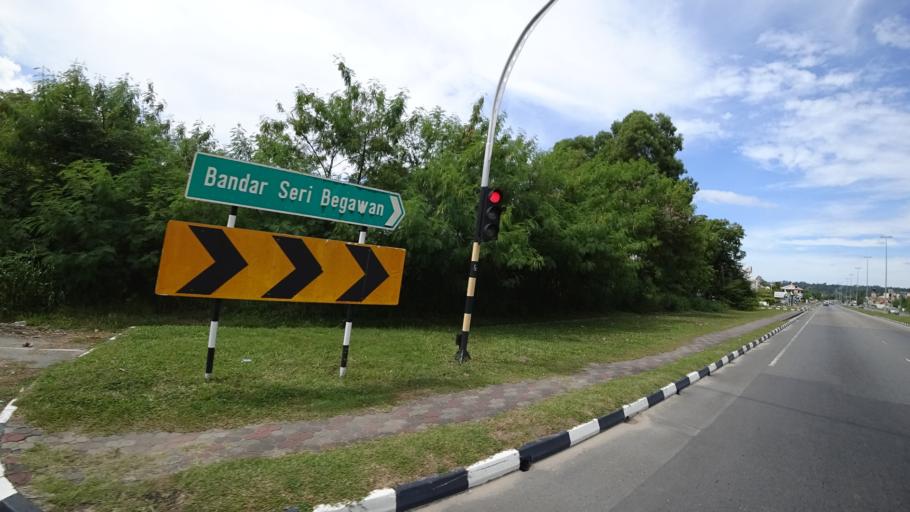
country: BN
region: Brunei and Muara
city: Bandar Seri Begawan
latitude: 4.8898
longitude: 114.8447
